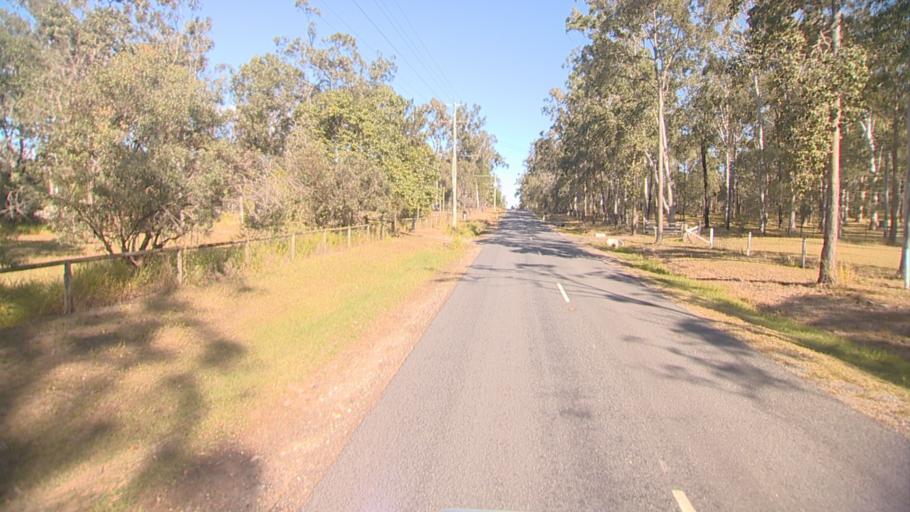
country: AU
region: Queensland
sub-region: Logan
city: Chambers Flat
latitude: -27.8078
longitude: 153.0724
